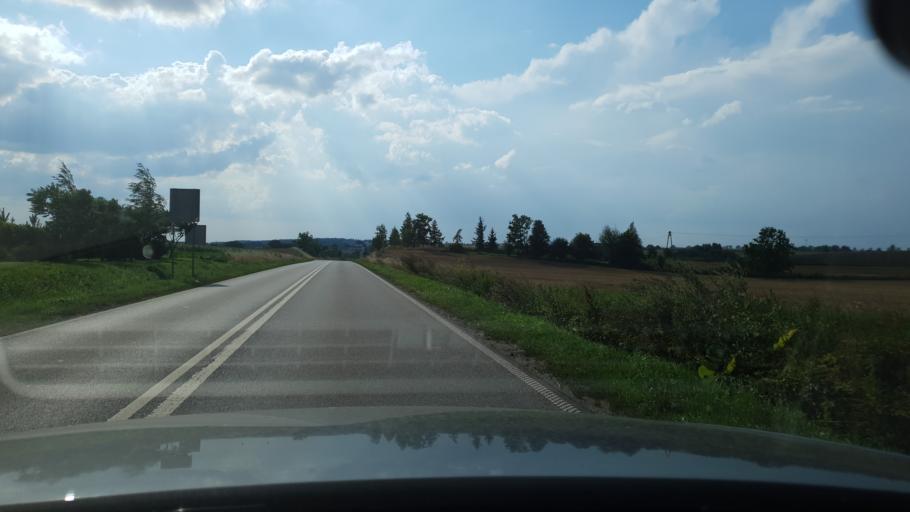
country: PL
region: Kujawsko-Pomorskie
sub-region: Powiat grudziadzki
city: Gruta
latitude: 53.4372
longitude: 18.8884
